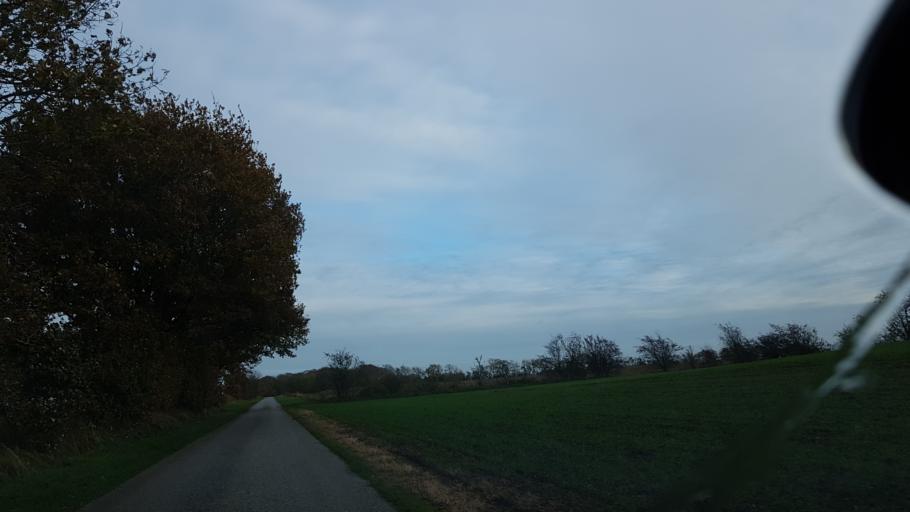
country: DK
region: South Denmark
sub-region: Haderslev Kommune
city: Vojens
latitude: 55.2992
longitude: 9.2594
